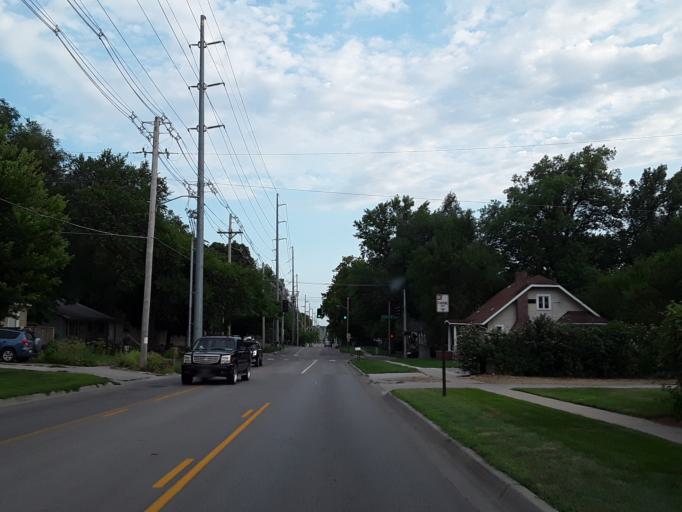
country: US
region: Nebraska
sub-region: Lancaster County
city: Lincoln
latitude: 40.8362
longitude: -96.6442
